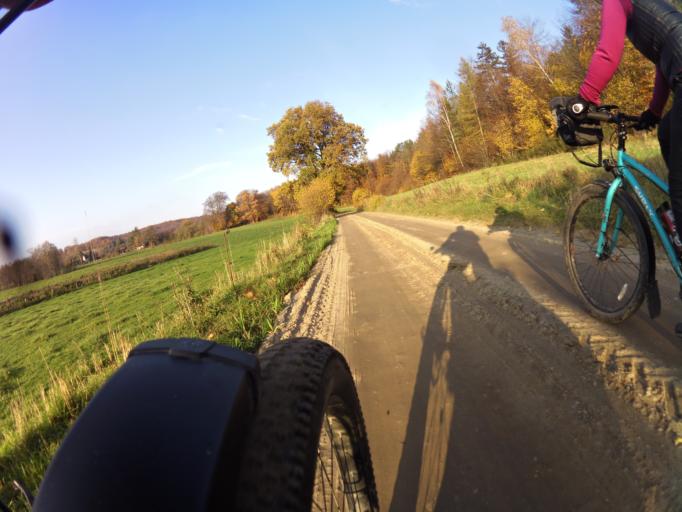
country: PL
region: Pomeranian Voivodeship
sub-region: Powiat pucki
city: Krokowa
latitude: 54.7478
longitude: 18.1954
